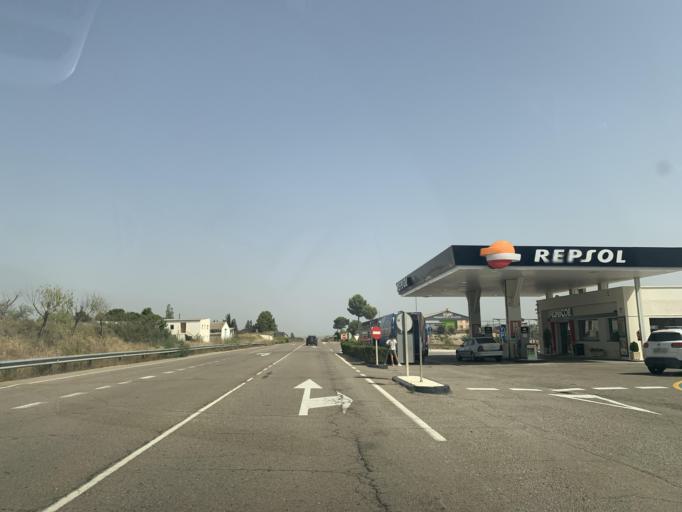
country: ES
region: Aragon
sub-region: Provincia de Zaragoza
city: Belchite
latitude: 41.3094
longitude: -0.7427
